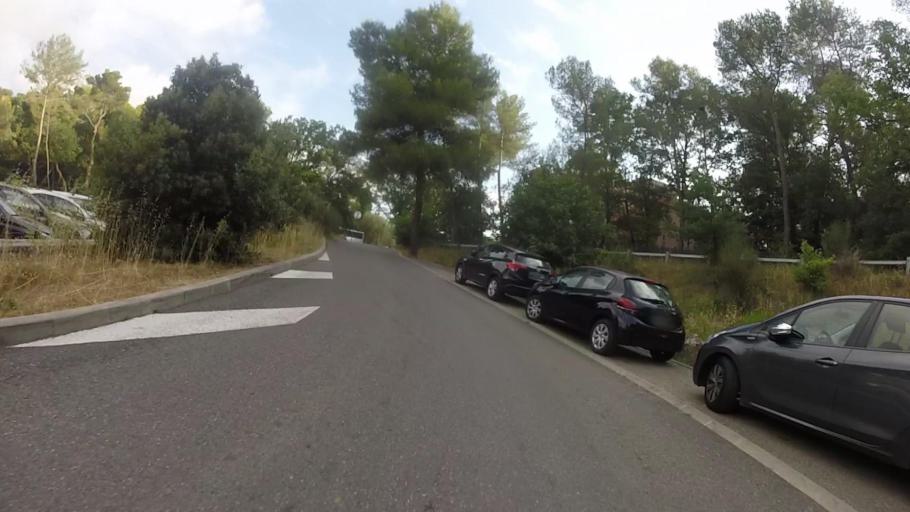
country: FR
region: Provence-Alpes-Cote d'Azur
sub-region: Departement des Alpes-Maritimes
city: Vallauris
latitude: 43.6215
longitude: 7.0444
